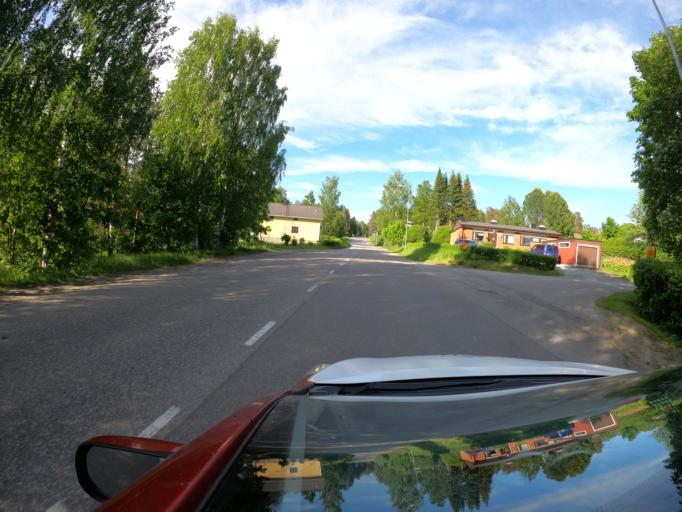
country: FI
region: Southern Savonia
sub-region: Savonlinna
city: Savonlinna
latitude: 61.8478
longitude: 28.9605
